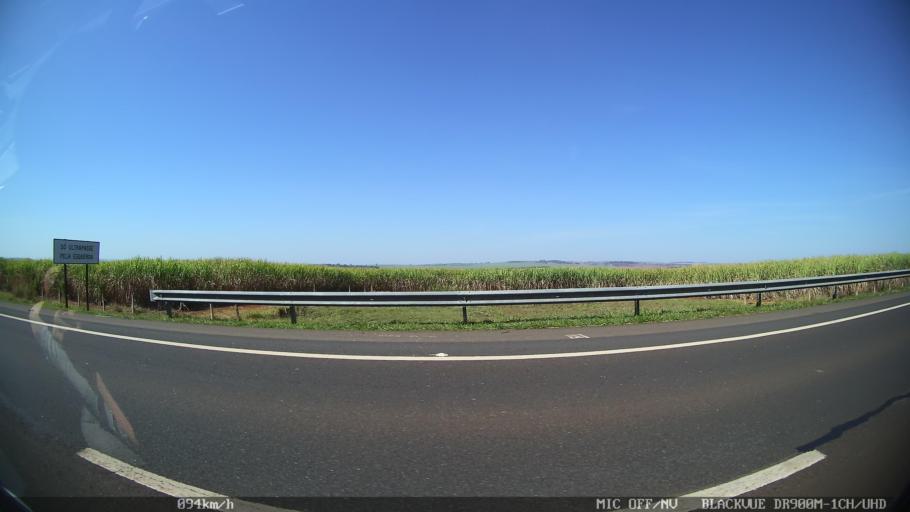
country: BR
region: Sao Paulo
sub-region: Batatais
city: Batatais
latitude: -20.7657
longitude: -47.5357
